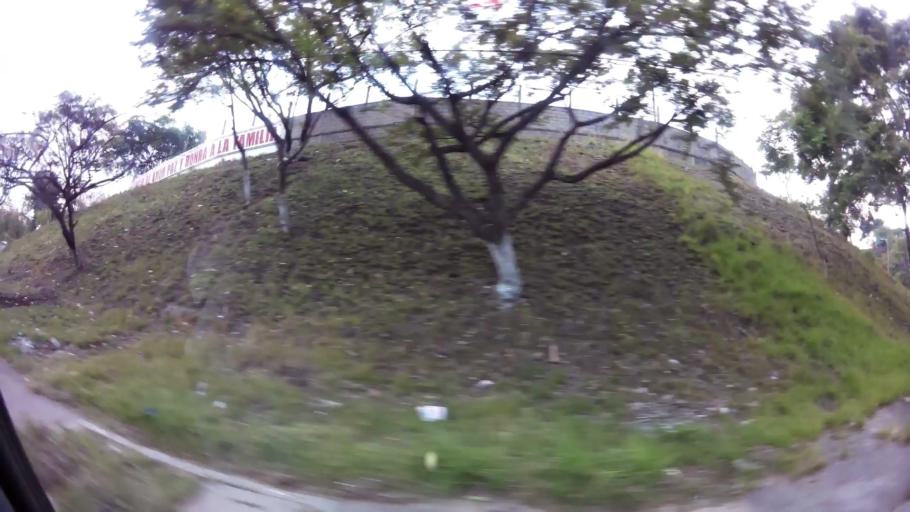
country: HN
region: Francisco Morazan
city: El Lolo
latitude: 14.1037
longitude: -87.2417
